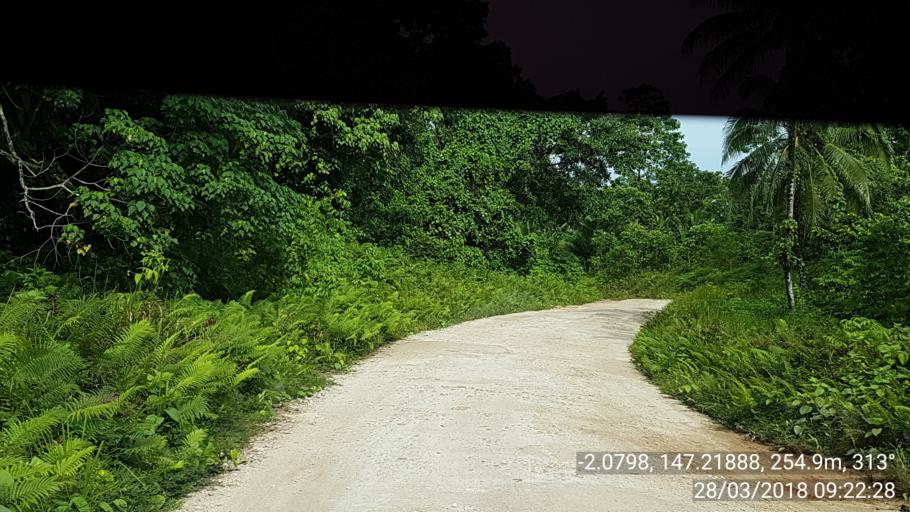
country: PG
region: Manus
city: Lorengau
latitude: -2.0797
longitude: 147.2189
